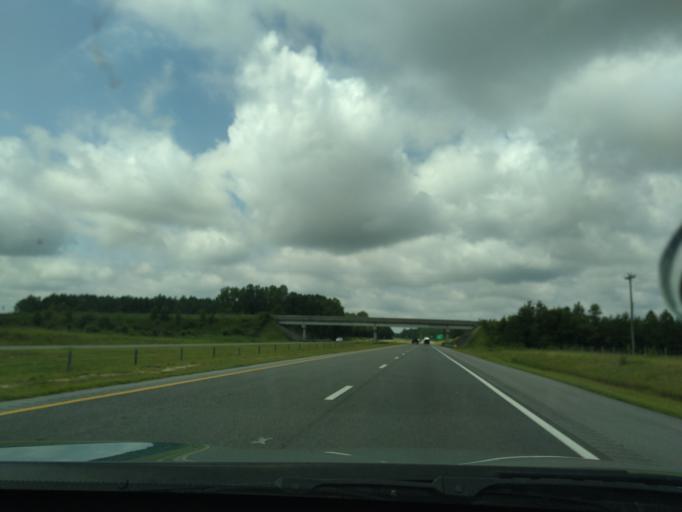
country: US
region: North Carolina
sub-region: Martin County
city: Robersonville
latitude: 35.8417
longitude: -77.2306
